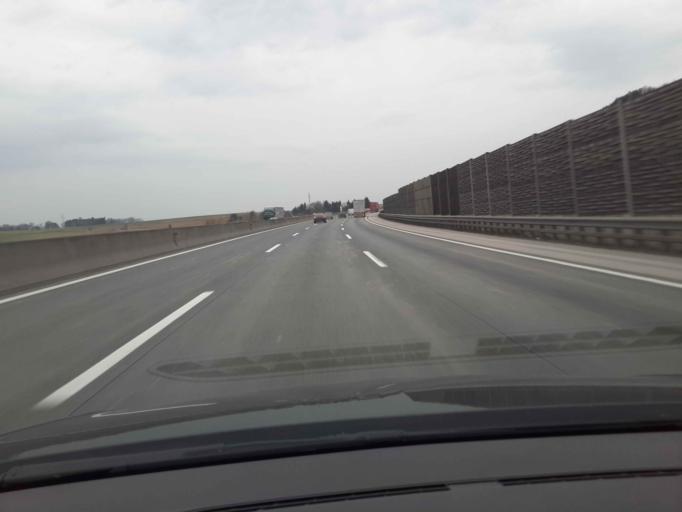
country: AT
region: Lower Austria
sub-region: Politischer Bezirk Melk
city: Loosdorf
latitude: 48.1994
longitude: 15.3700
